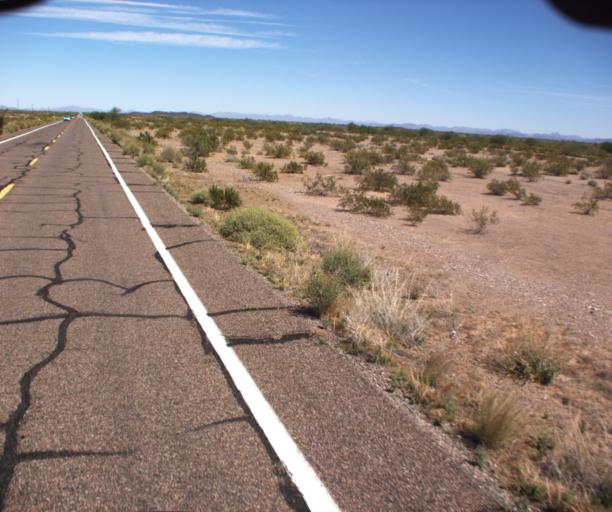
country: US
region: Arizona
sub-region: Maricopa County
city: Gila Bend
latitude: 32.7716
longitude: -112.8154
